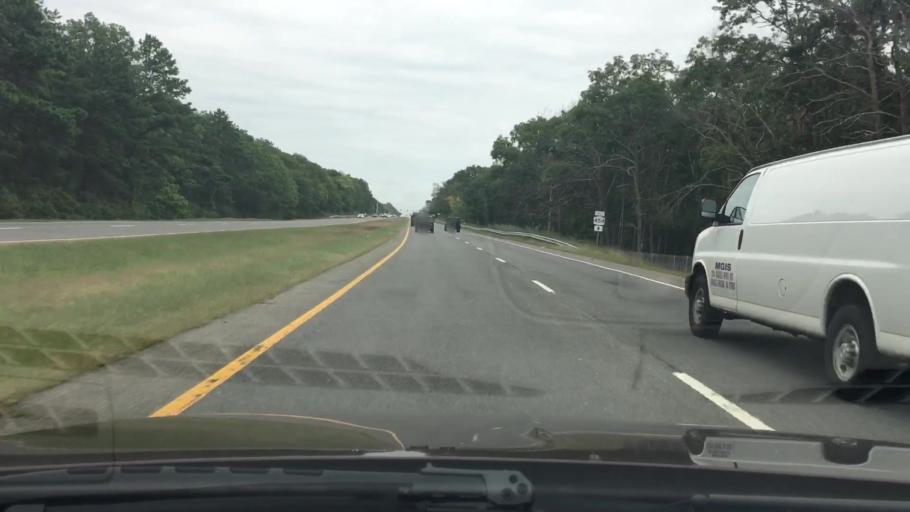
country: US
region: New York
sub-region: Suffolk County
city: Islandia
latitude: 40.7896
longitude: -73.1528
